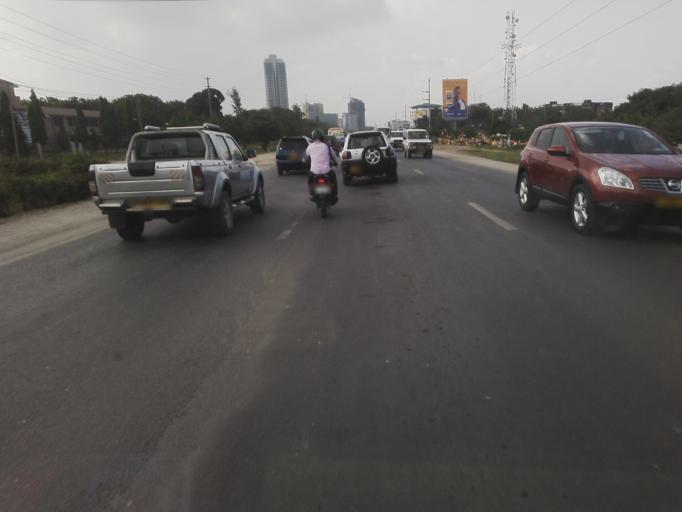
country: TZ
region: Dar es Salaam
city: Magomeni
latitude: -6.7715
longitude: 39.2385
